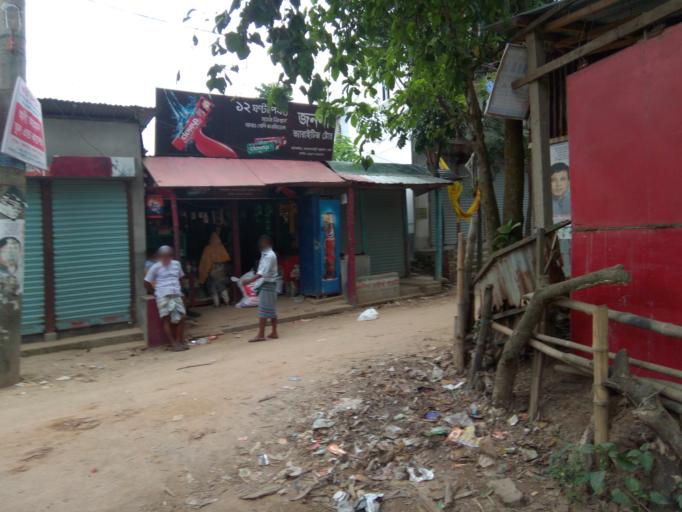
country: BD
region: Dhaka
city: Paltan
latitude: 23.7389
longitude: 90.4618
